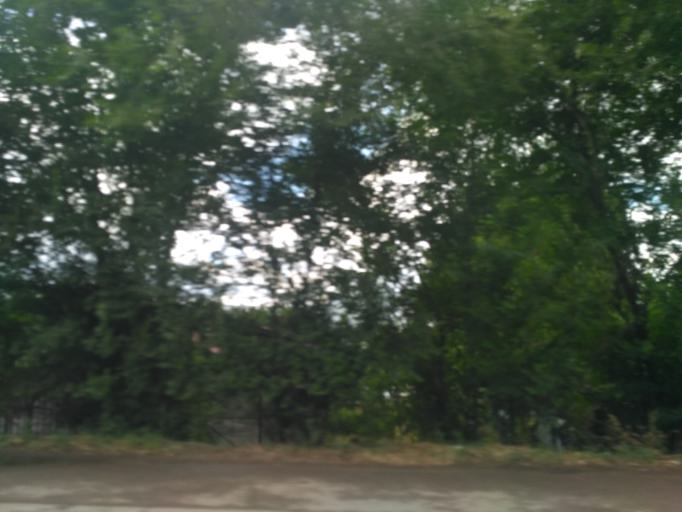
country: KZ
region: Almaty Oblysy
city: Burunday
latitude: 43.2005
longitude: 76.6312
